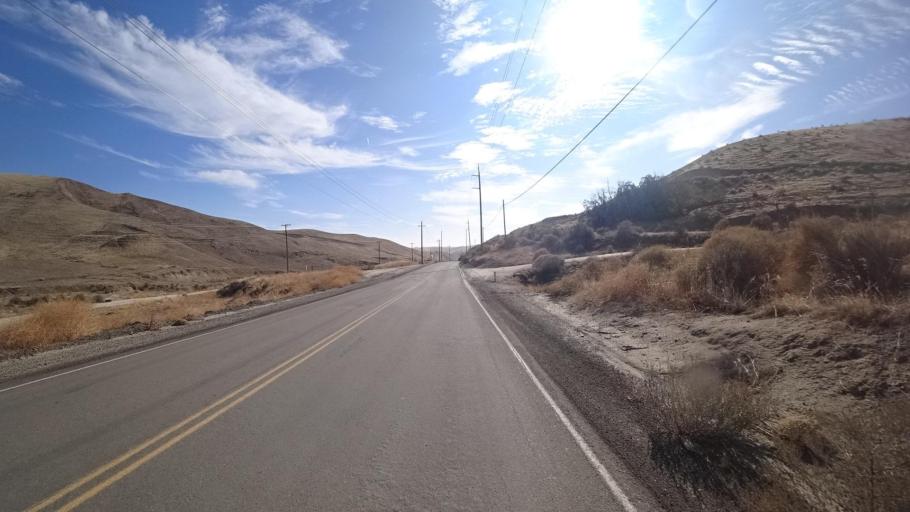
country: US
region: California
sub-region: Kern County
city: Oildale
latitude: 35.5554
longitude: -118.9587
